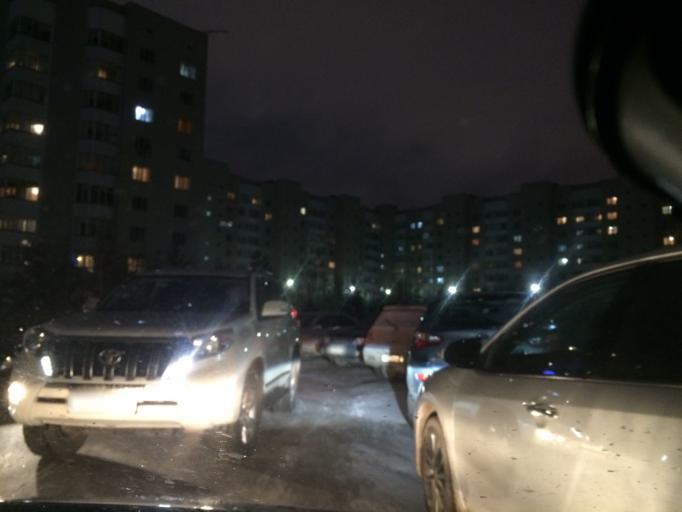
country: KZ
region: Astana Qalasy
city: Astana
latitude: 51.1207
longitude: 71.4179
